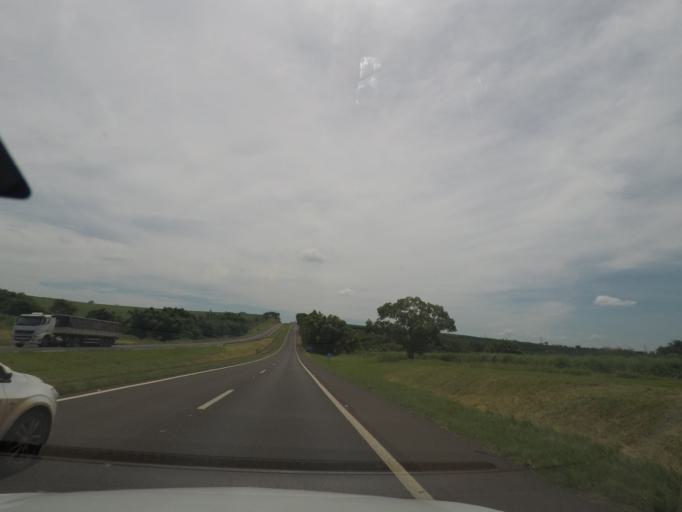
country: BR
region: Sao Paulo
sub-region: Bebedouro
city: Bebedouro
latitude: -21.0302
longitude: -48.4208
